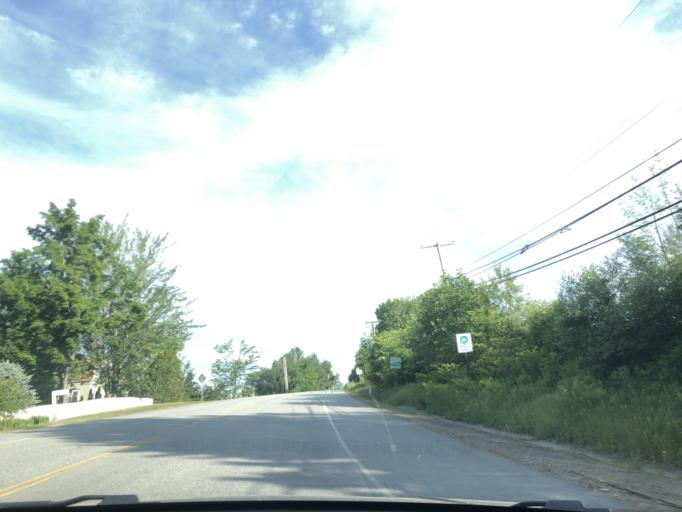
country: US
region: New Hampshire
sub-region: Merrimack County
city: New London
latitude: 43.3998
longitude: -71.9632
